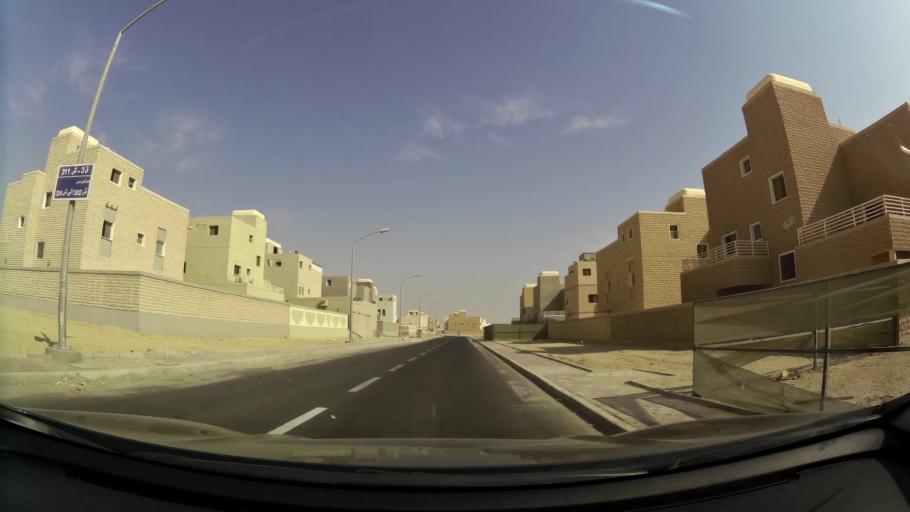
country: KW
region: Al Ahmadi
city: Al Wafrah
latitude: 28.8020
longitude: 48.0676
